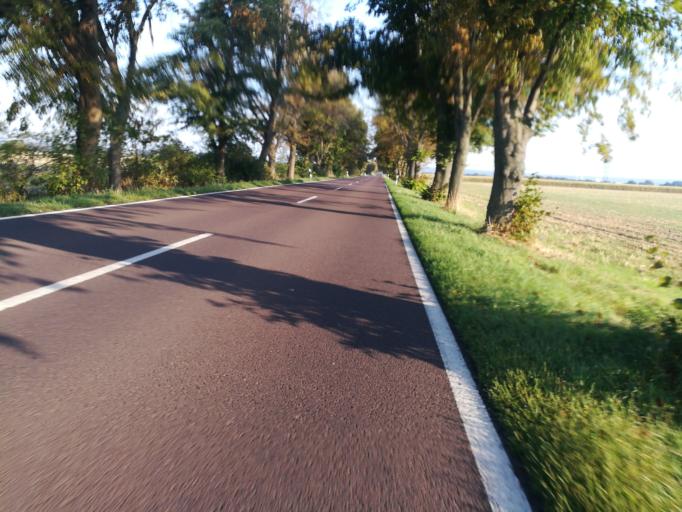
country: DE
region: Saxony-Anhalt
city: Gross Santersleben
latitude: 52.2407
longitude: 11.4399
